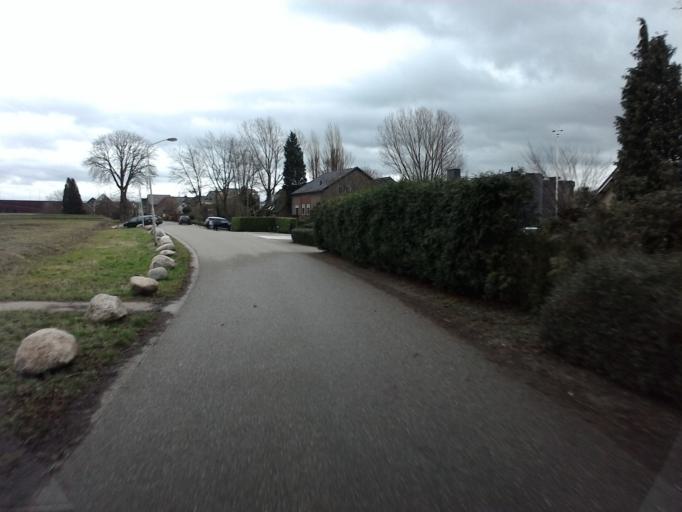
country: NL
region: Gelderland
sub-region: Gemeente Nijmegen
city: Nijmegen
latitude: 51.8544
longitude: 5.8626
